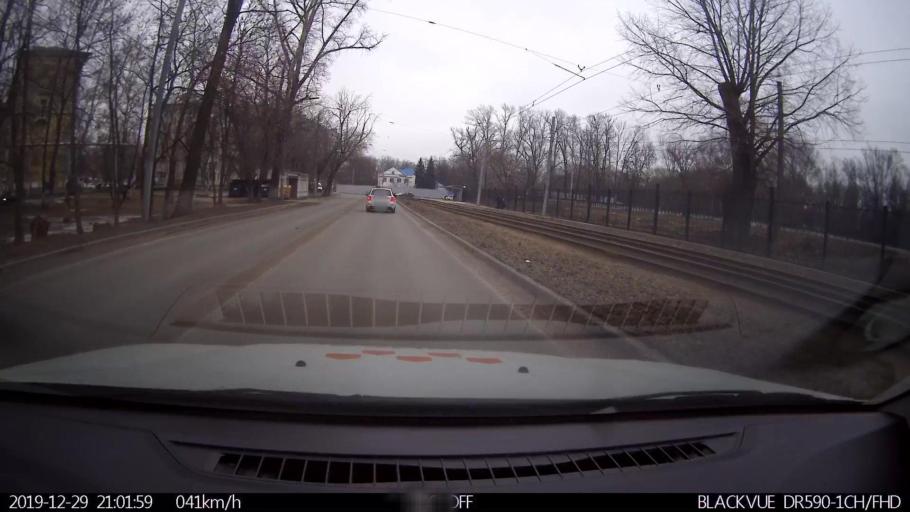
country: RU
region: Nizjnij Novgorod
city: Nizhniy Novgorod
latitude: 56.3112
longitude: 43.9291
